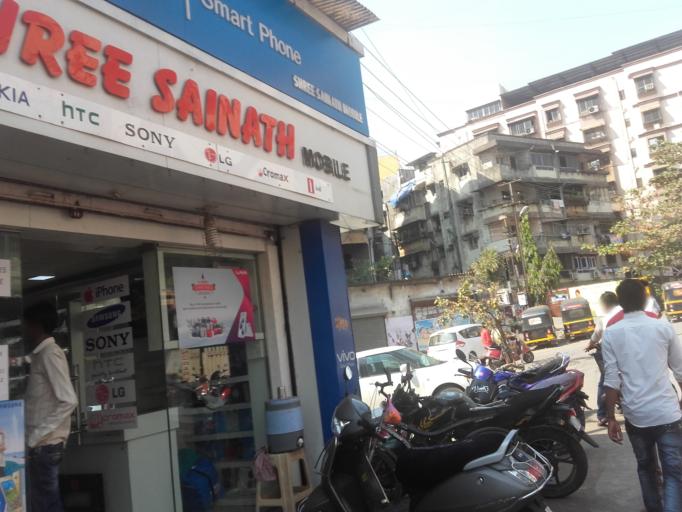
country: IN
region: Maharashtra
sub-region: Thane
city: Ulhasnagar
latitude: 19.2293
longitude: 73.1593
